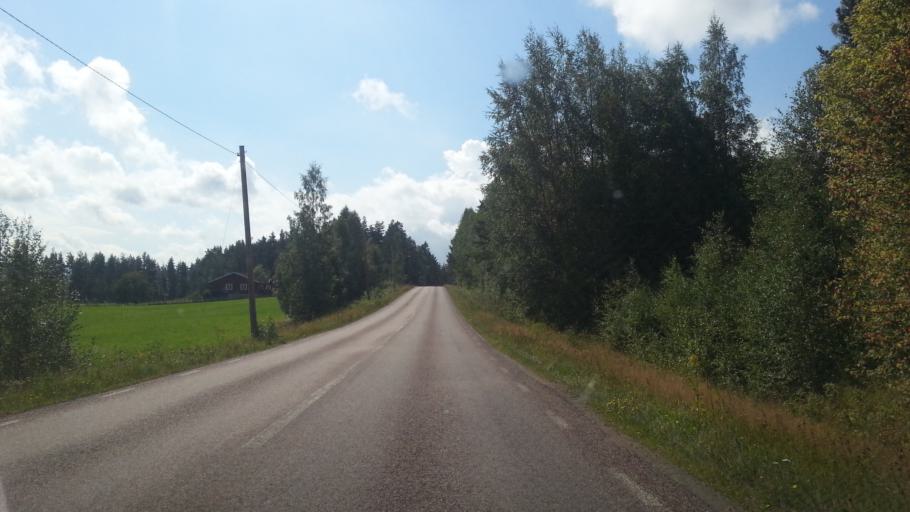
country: SE
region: Dalarna
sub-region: Faluns Kommun
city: Falun
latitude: 60.6204
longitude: 15.7667
